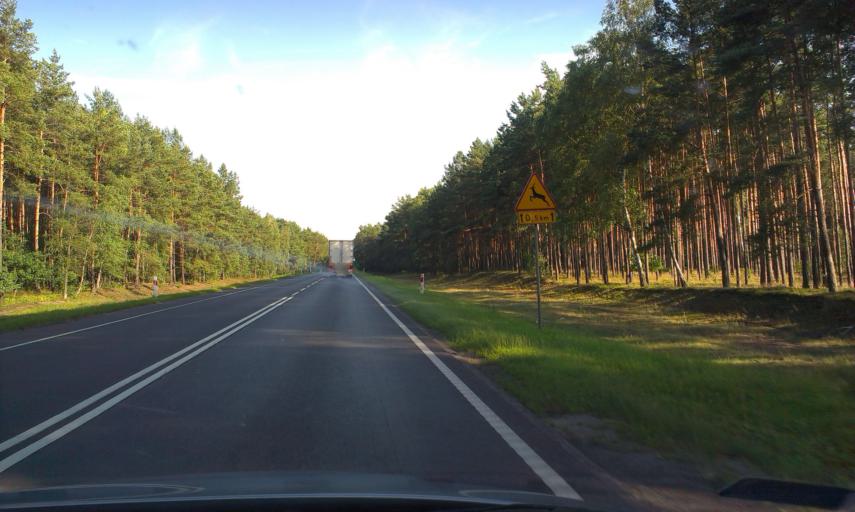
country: PL
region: Kujawsko-Pomorskie
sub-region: Powiat bydgoski
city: Biale Blota
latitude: 53.1059
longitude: 17.8863
